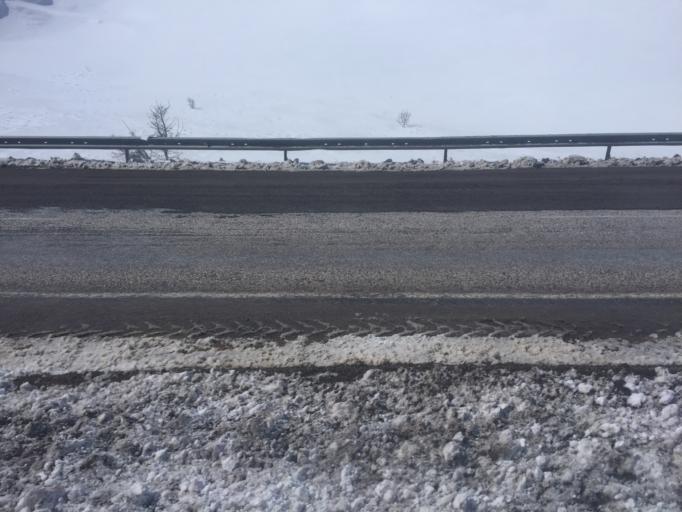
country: TR
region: Kahramanmaras
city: Goksun
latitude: 38.1967
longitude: 36.4562
